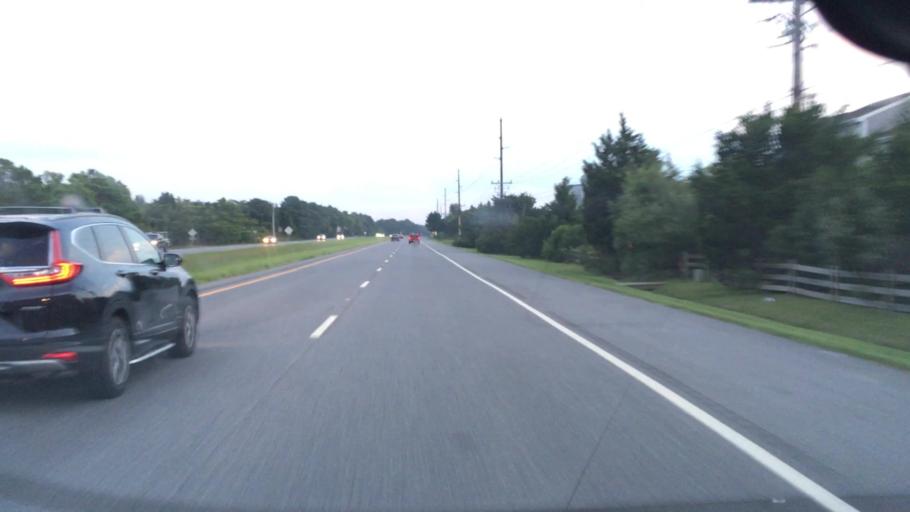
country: US
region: Delaware
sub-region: Sussex County
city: Bethany Beach
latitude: 38.5820
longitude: -75.0614
